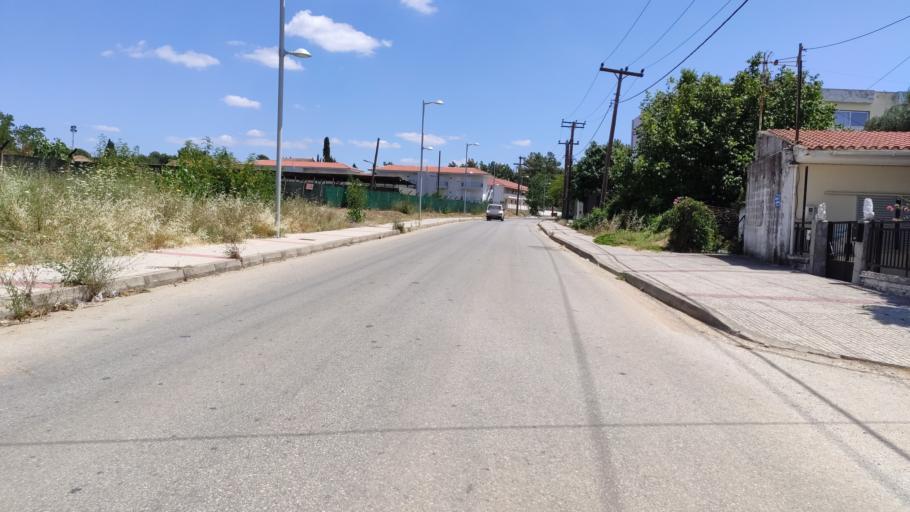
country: GR
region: East Macedonia and Thrace
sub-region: Nomos Rodopis
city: Komotini
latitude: 41.1301
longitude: 25.4063
